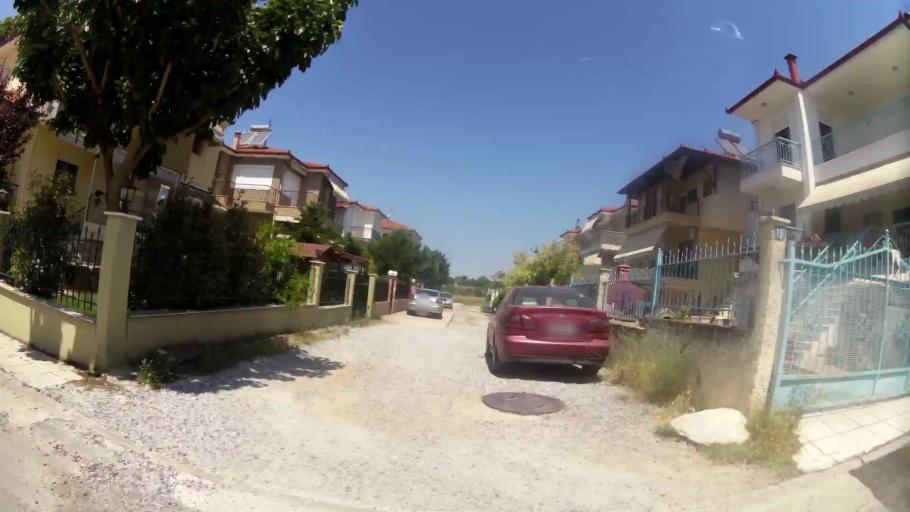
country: GR
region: Central Macedonia
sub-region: Nomos Thessalonikis
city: Nea Michaniona
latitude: 40.4769
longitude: 22.8681
